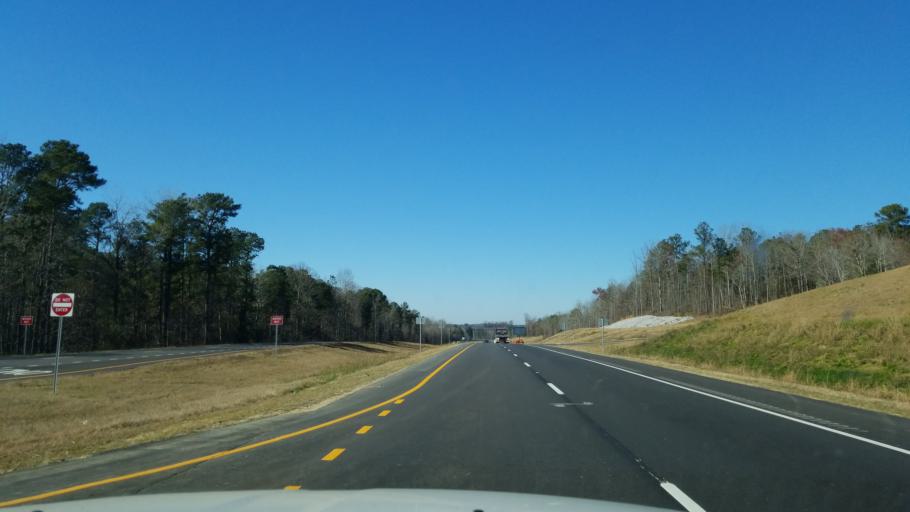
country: US
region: Alabama
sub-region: Pickens County
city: Reform
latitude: 33.3604
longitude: -87.9731
